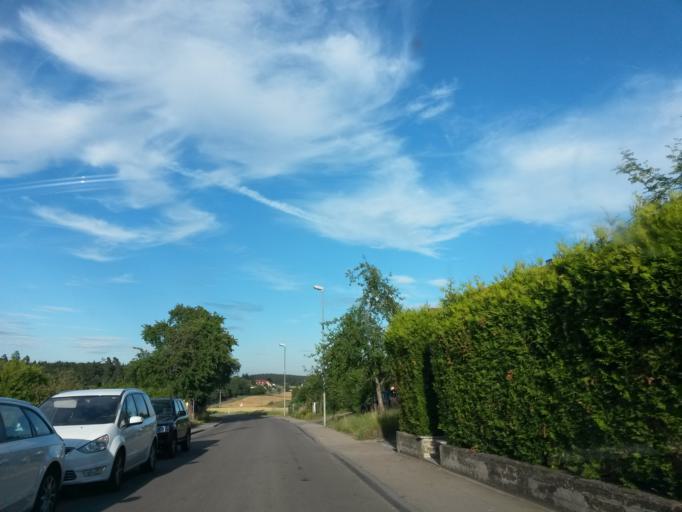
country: DE
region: Baden-Wuerttemberg
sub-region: Regierungsbezirk Stuttgart
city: Ellenberg
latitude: 49.0530
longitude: 10.2081
